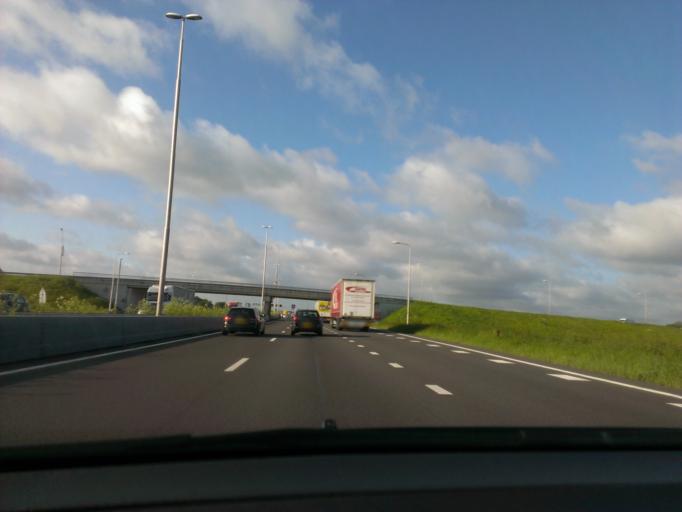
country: NL
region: Limburg
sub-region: Gemeente Sittard-Geleen
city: Born
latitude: 51.0742
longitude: 5.8246
